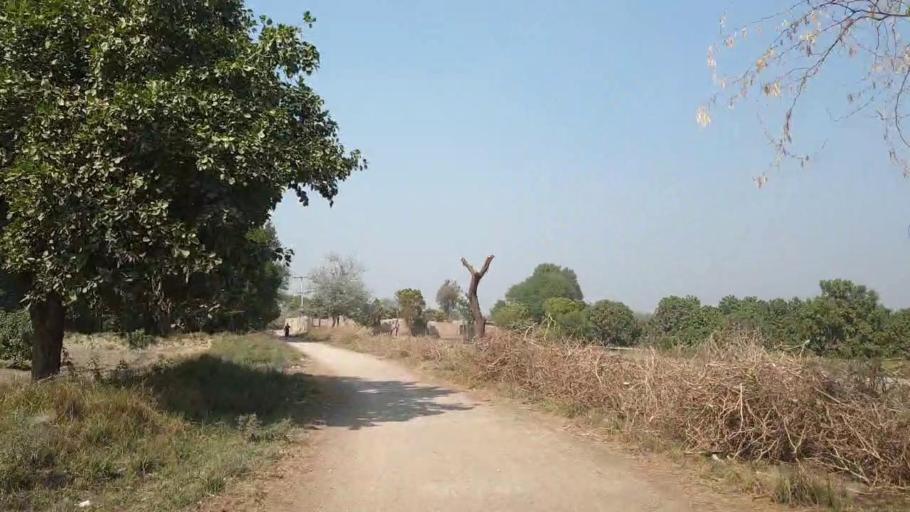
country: PK
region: Sindh
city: Tando Allahyar
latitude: 25.4837
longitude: 68.8010
